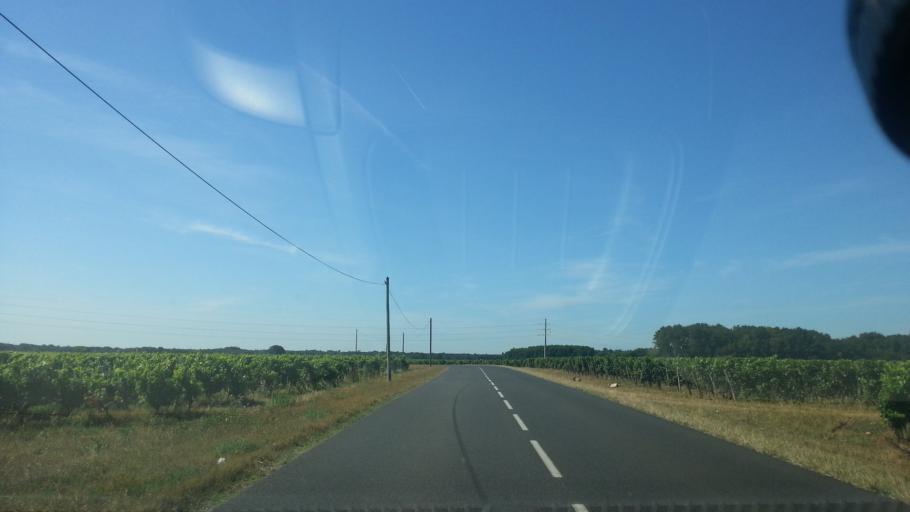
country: FR
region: Aquitaine
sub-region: Departement de la Gironde
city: Podensac
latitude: 44.6397
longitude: -0.3624
